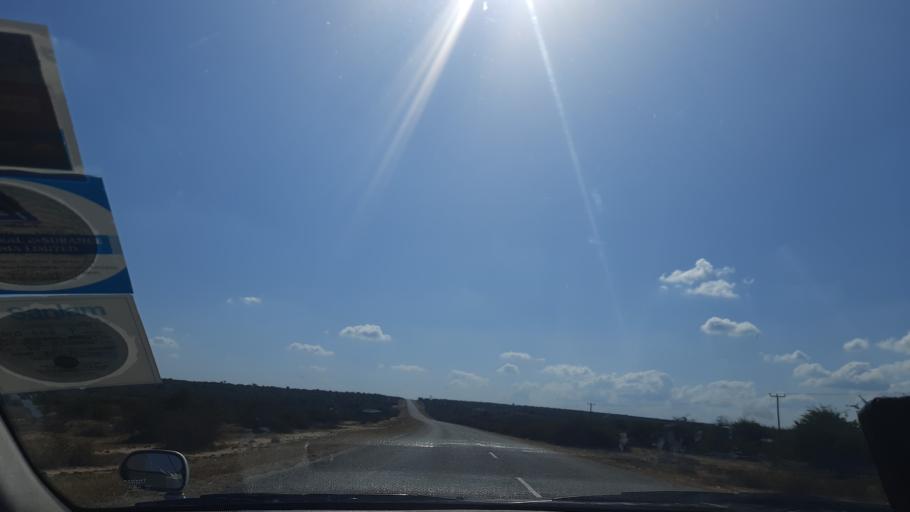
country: TZ
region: Singida
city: Kilimatinde
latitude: -5.7272
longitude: 34.7890
